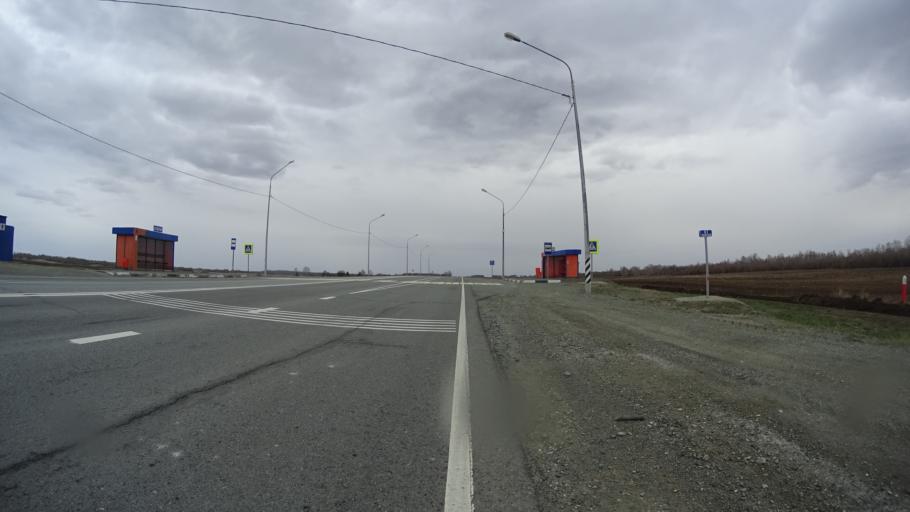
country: RU
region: Chelyabinsk
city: Krasnogorskiy
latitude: 54.6722
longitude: 61.2499
